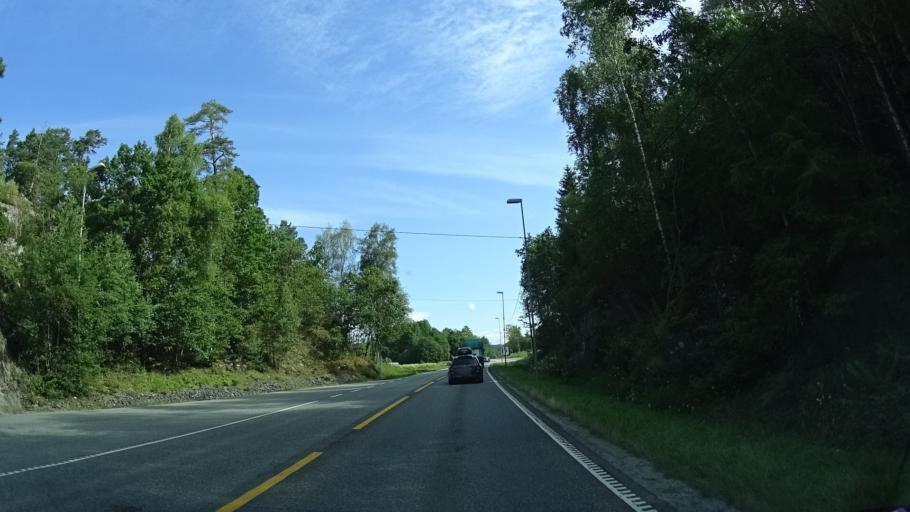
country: NO
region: Telemark
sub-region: Bamble
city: Langesund
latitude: 59.0029
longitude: 9.6546
